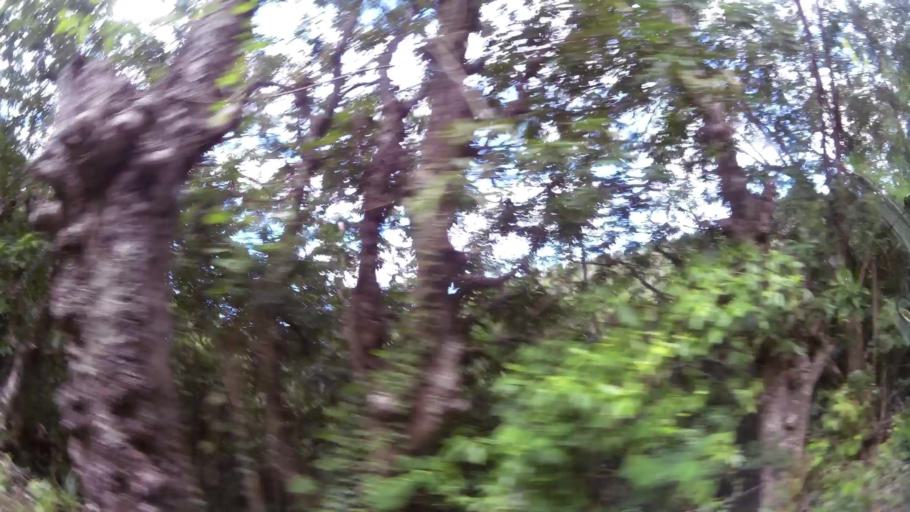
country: DM
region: Saint John
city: Portsmouth
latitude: 15.6187
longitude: -61.4633
